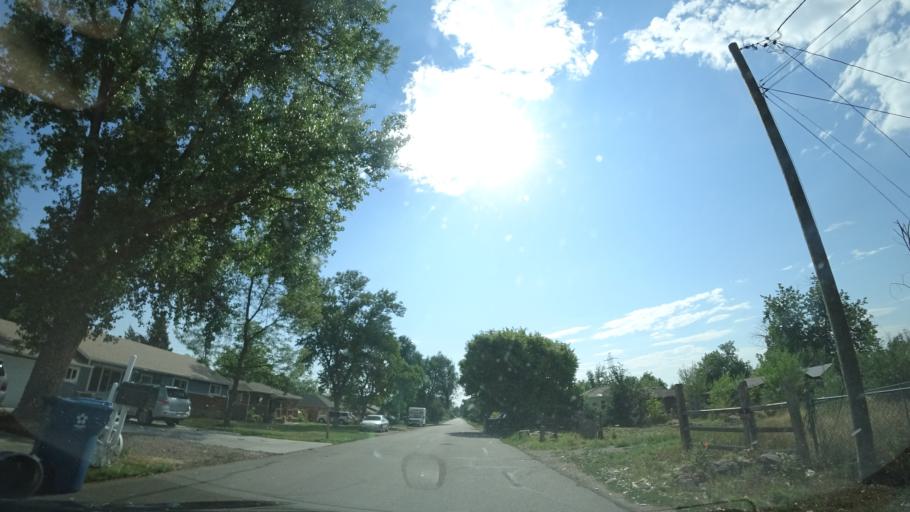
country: US
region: Colorado
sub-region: Jefferson County
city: Lakewood
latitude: 39.7211
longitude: -105.0625
